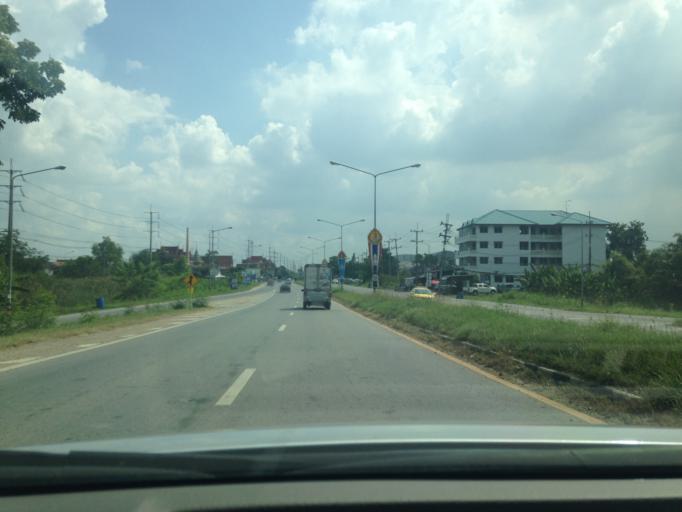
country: TH
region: Pathum Thani
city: Sam Khok
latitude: 14.0827
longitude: 100.5202
